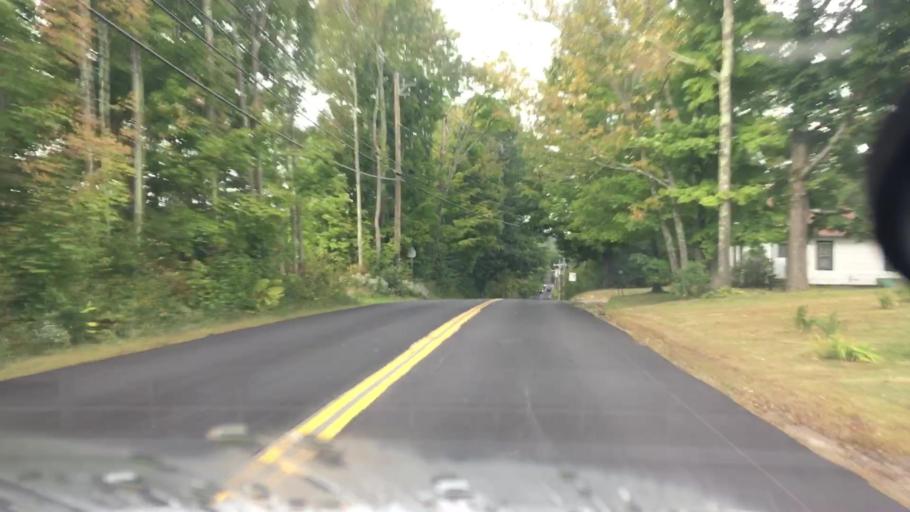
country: US
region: New Hampshire
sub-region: Carroll County
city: Wakefield
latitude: 43.5697
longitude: -71.0280
